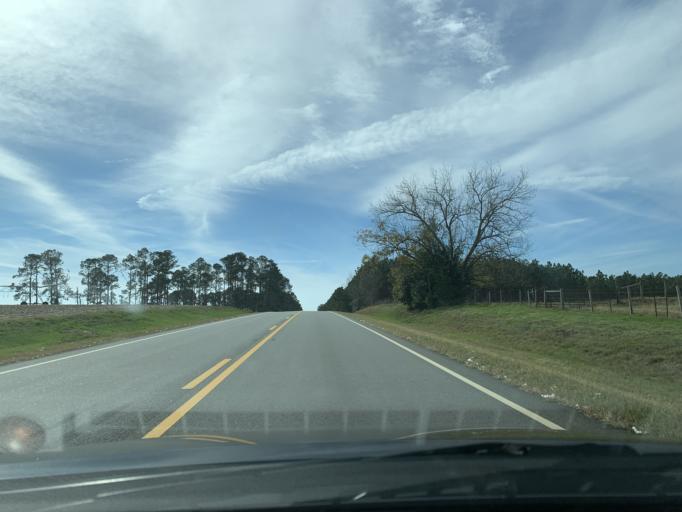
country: US
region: Georgia
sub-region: Turner County
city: Ashburn
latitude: 31.7827
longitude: -83.5128
